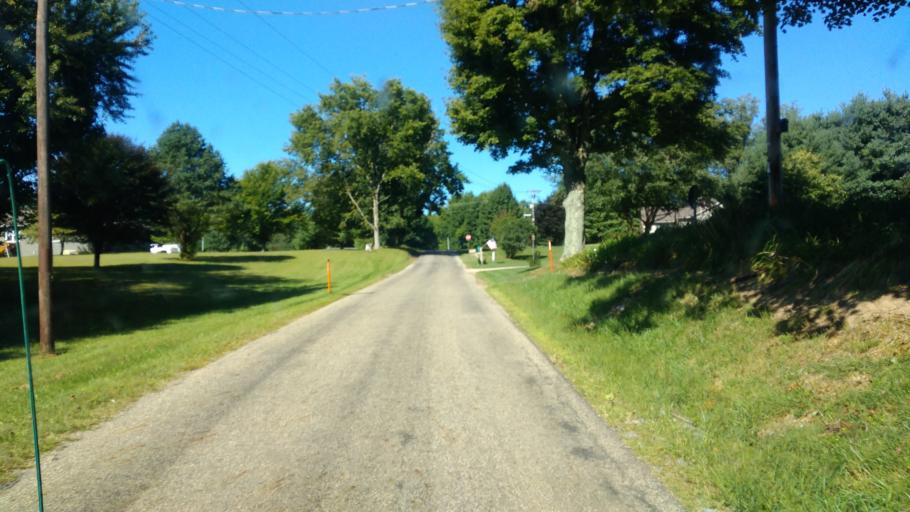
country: US
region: Ohio
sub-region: Knox County
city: Mount Vernon
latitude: 40.4548
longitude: -82.4849
